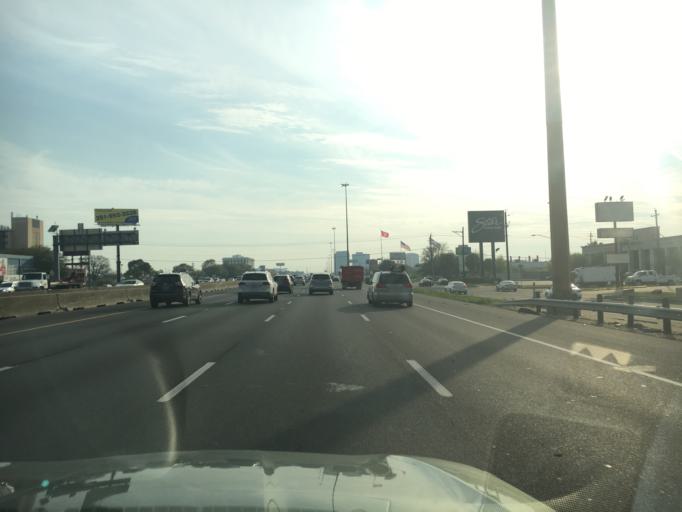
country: US
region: Texas
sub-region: Harris County
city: Bellaire
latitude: 29.7134
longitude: -95.5032
